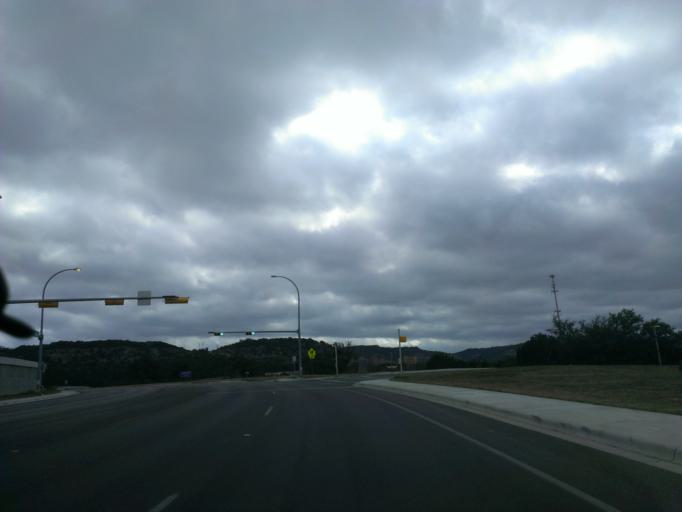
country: US
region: Texas
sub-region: Travis County
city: The Hills
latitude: 30.3388
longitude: -98.0269
